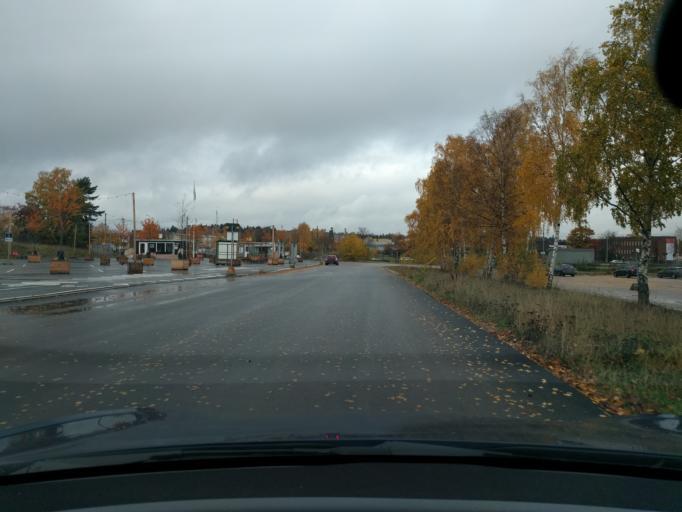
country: SE
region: Stockholm
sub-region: Taby Kommun
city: Taby
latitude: 59.4458
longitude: 18.0854
